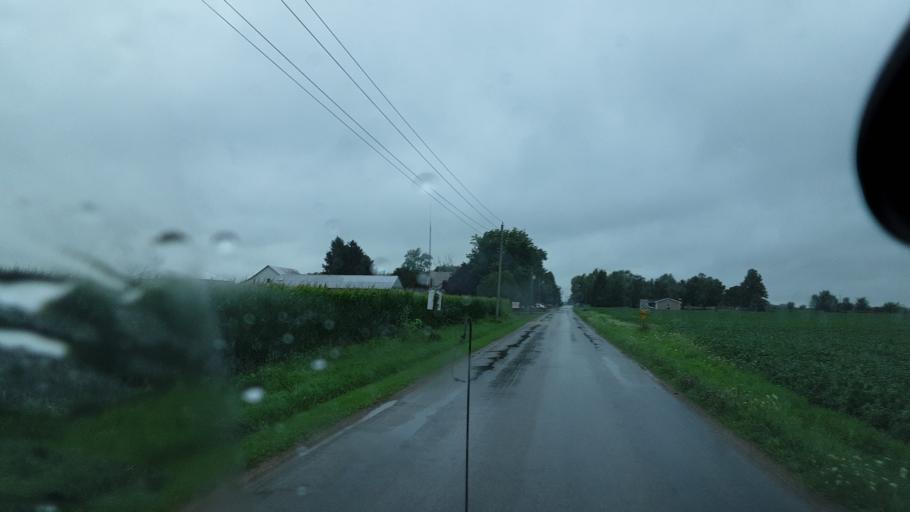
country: US
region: Indiana
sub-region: Adams County
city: Berne
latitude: 40.7135
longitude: -84.8533
